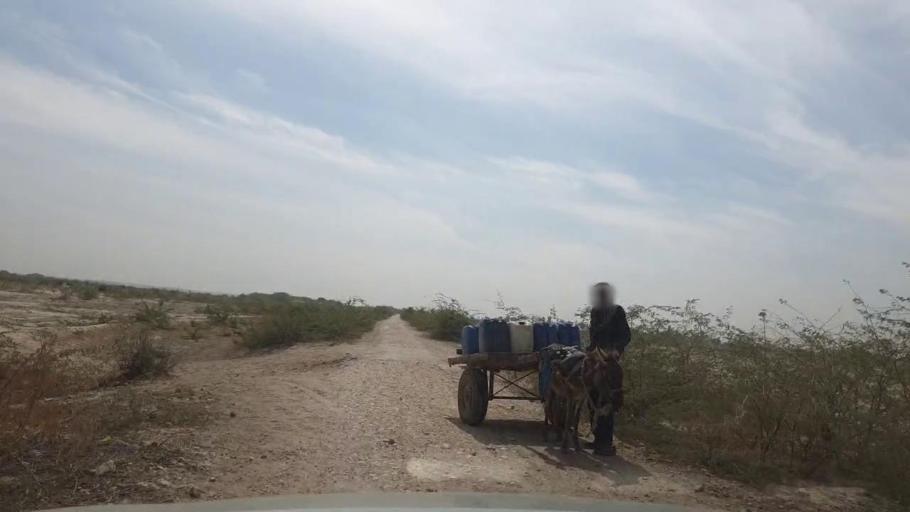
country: PK
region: Sindh
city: Nabisar
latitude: 25.0785
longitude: 69.5988
